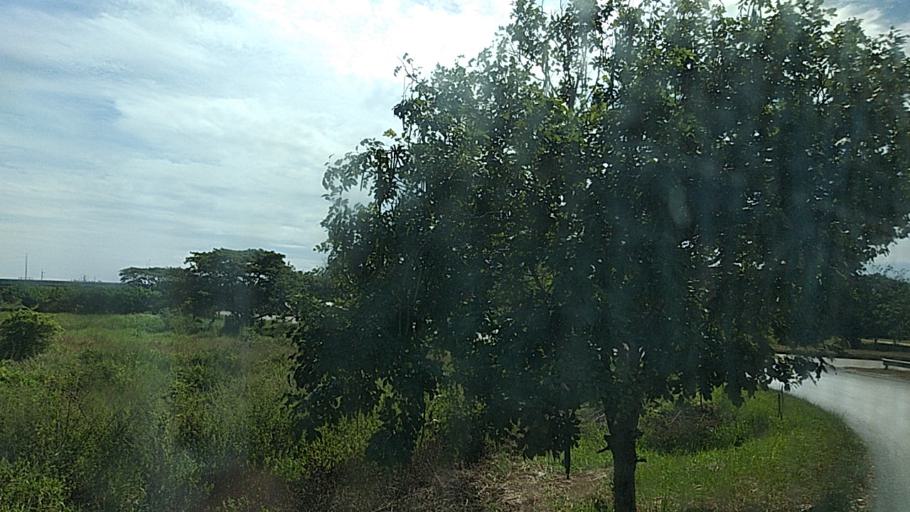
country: TH
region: Khon Kaen
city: Khon Kaen
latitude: 16.4381
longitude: 102.9152
